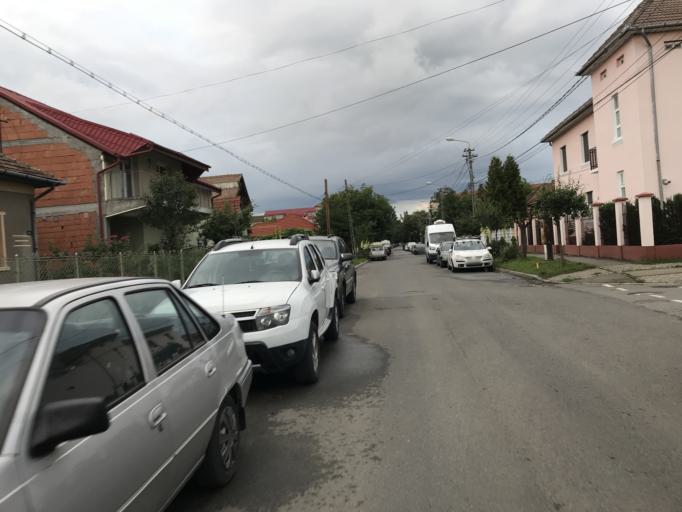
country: RO
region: Timis
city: Timisoara
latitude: 45.7743
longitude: 21.2354
